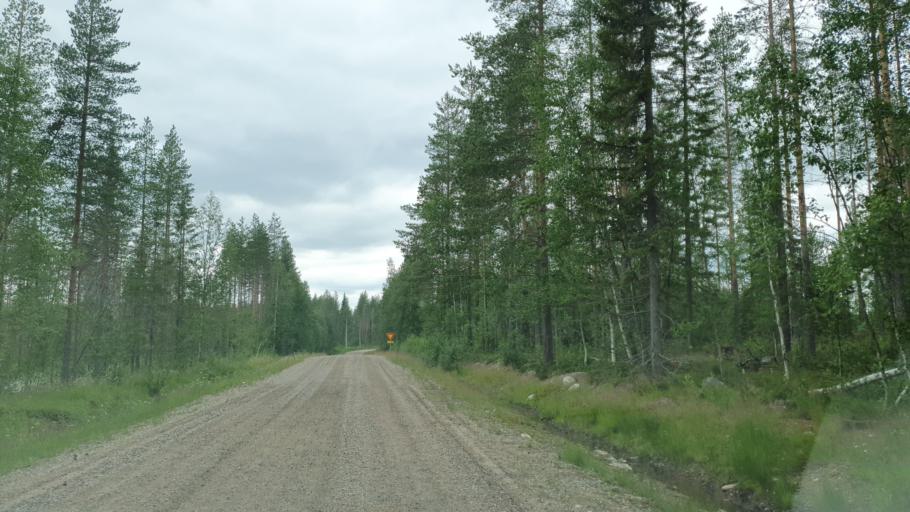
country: FI
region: Kainuu
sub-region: Kehys-Kainuu
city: Kuhmo
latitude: 64.0112
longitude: 29.3431
